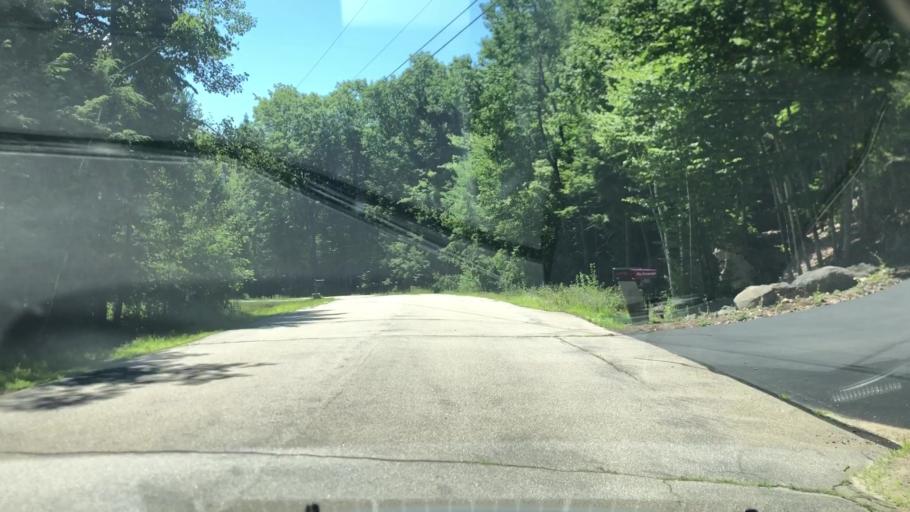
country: US
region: New Hampshire
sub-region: Hillsborough County
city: Mont Vernon
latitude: 42.9029
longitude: -71.6099
